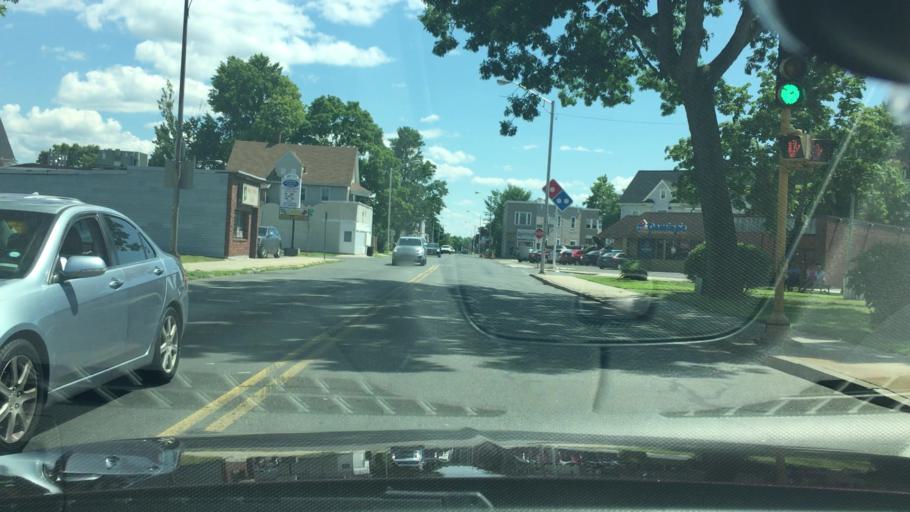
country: US
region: Massachusetts
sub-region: Hampden County
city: Springfield
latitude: 42.1252
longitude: -72.5844
